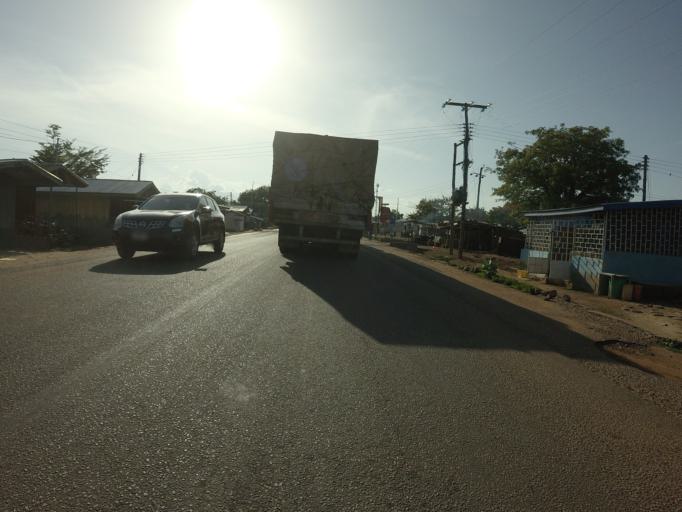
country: GH
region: Upper East
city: Navrongo
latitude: 10.8956
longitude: -1.0846
